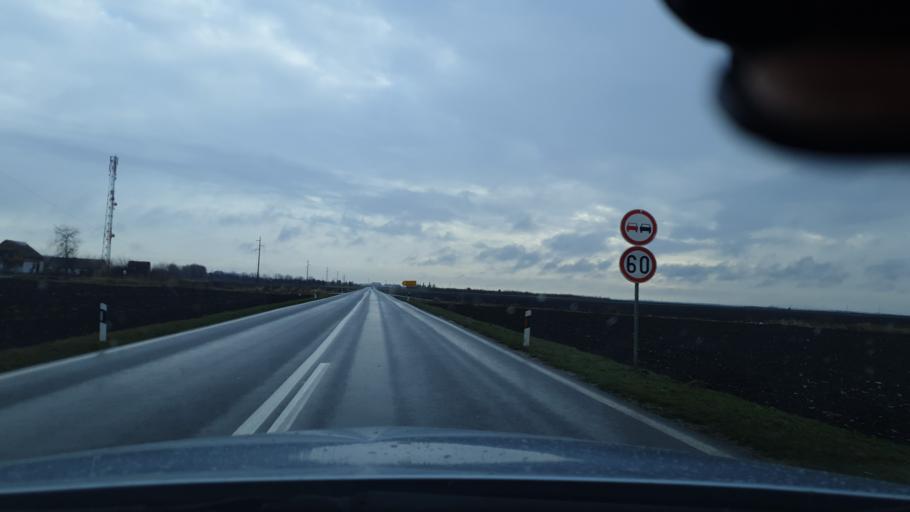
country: RS
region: Autonomna Pokrajina Vojvodina
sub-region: Juznobanatski Okrug
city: Kovin
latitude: 44.8099
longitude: 20.8614
